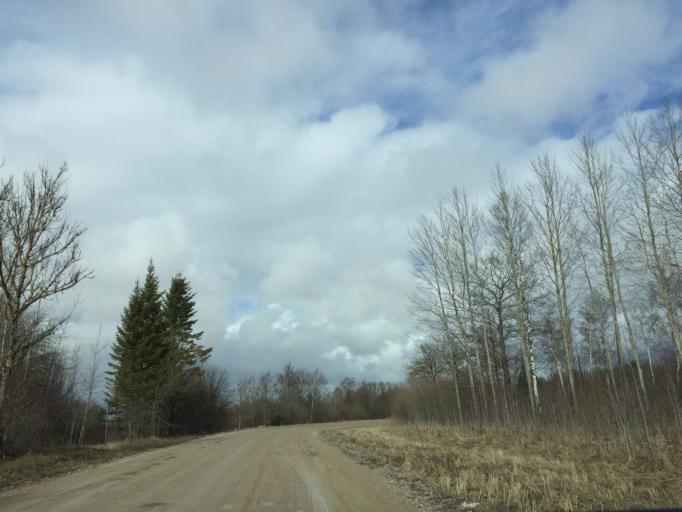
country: EE
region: Laeaene
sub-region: Lihula vald
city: Lihula
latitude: 58.7340
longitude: 23.8280
